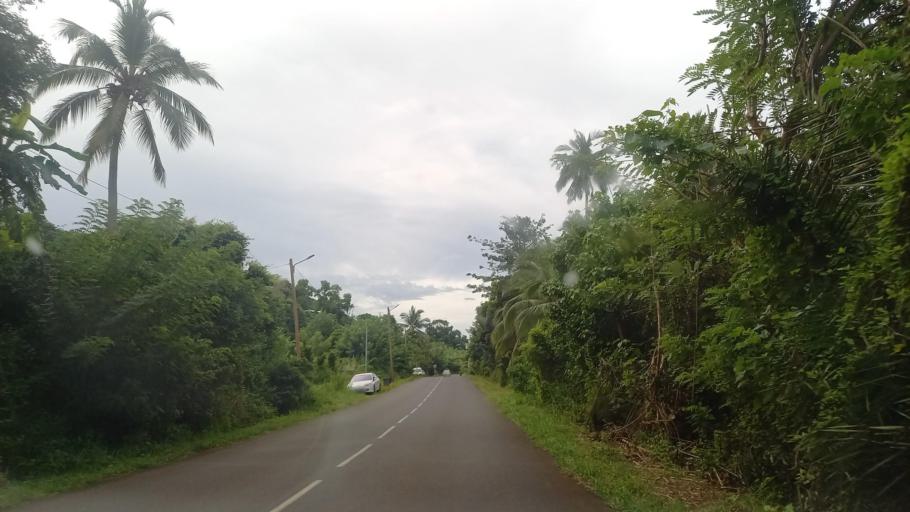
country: YT
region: Boueni
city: Boueni
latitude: -12.9086
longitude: 45.1011
